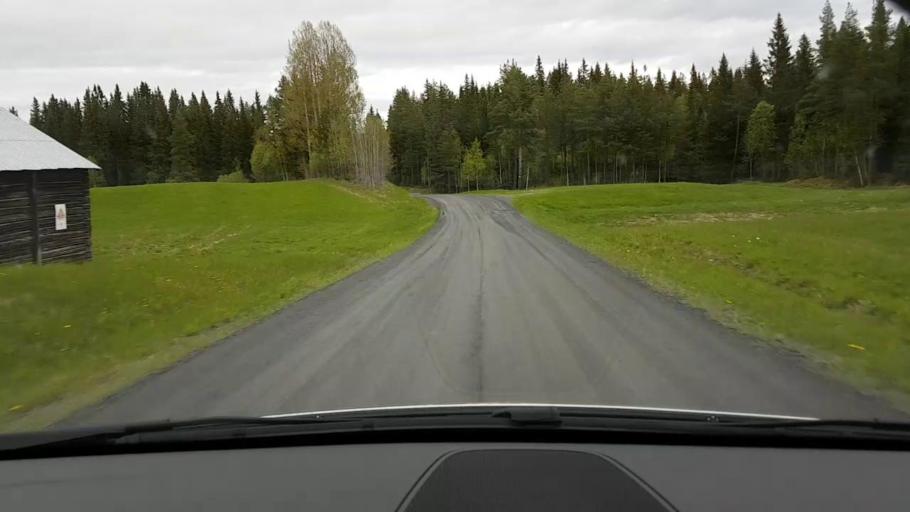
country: SE
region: Jaemtland
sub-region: Krokoms Kommun
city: Krokom
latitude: 63.3249
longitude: 14.4127
